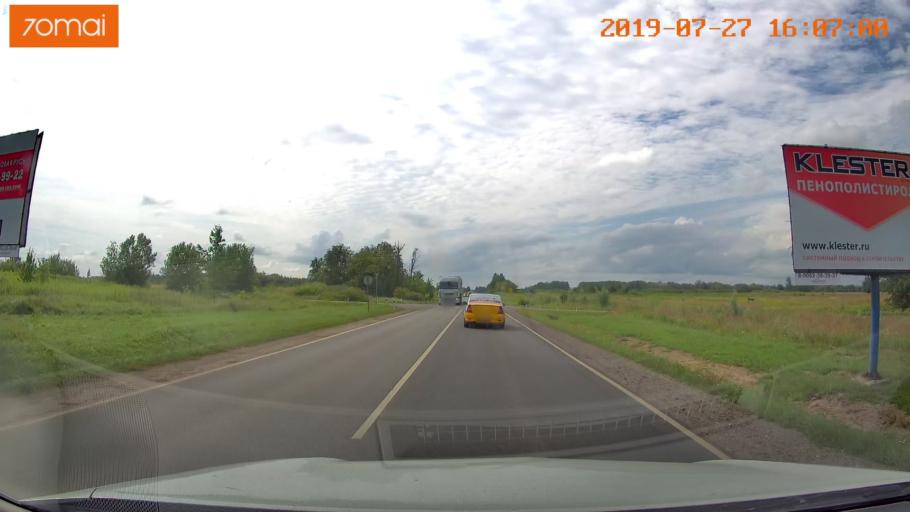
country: RU
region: Kaliningrad
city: Chernyakhovsk
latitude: 54.6347
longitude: 21.7669
